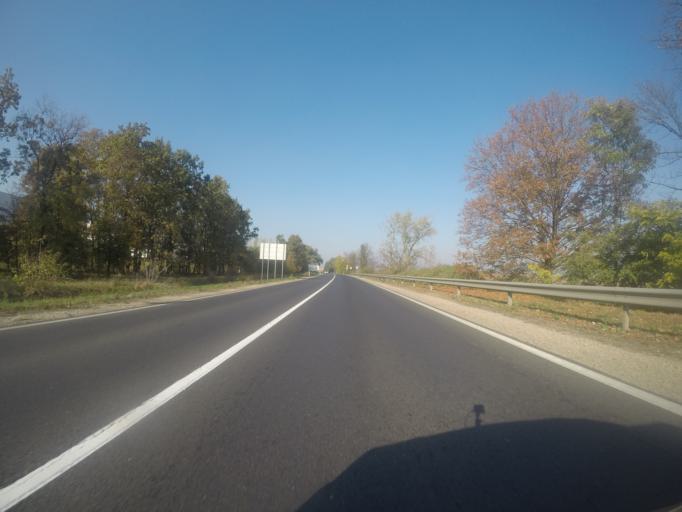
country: HU
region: Fejer
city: Racalmas
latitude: 47.0005
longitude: 18.9305
